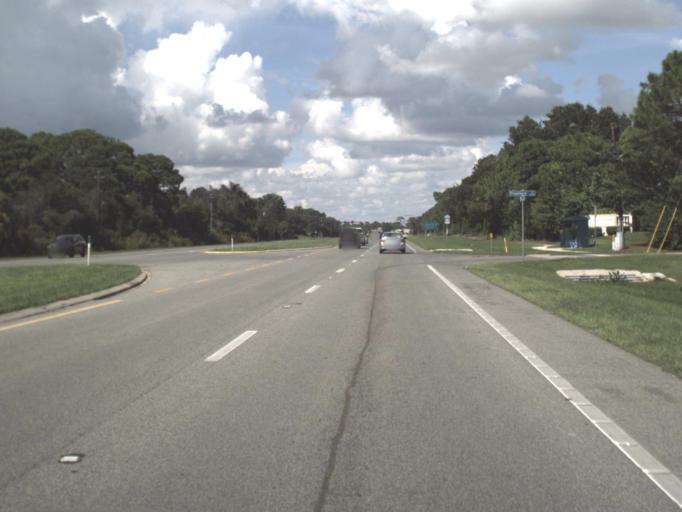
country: US
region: Florida
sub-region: Sarasota County
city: Vamo
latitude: 27.2106
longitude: -82.4902
